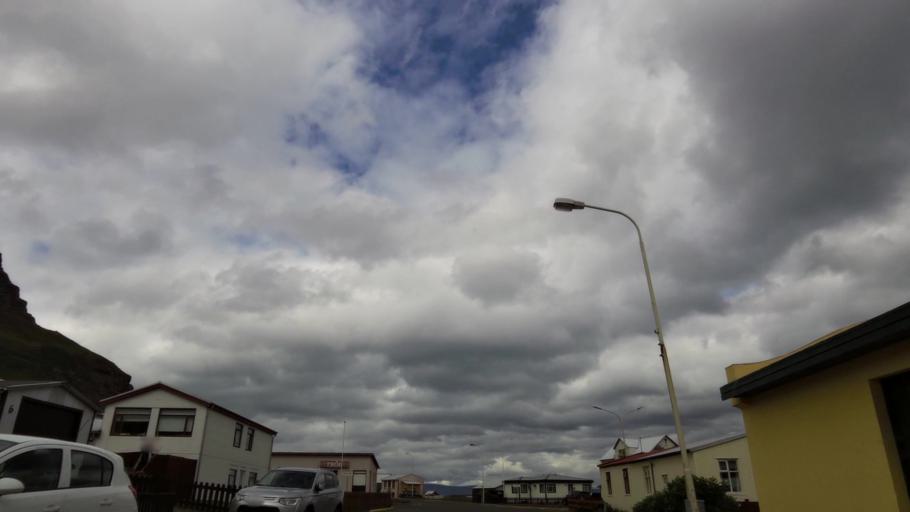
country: IS
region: Westfjords
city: Isafjoerdur
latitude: 66.1598
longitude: -23.2480
